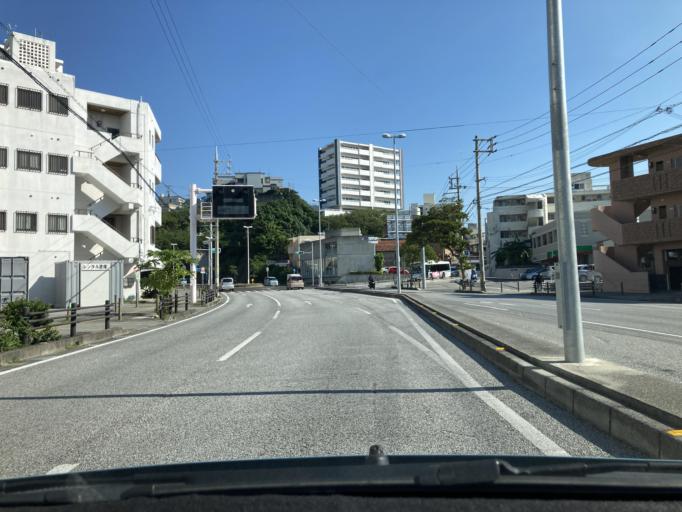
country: JP
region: Okinawa
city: Naha-shi
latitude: 26.2035
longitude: 127.7064
